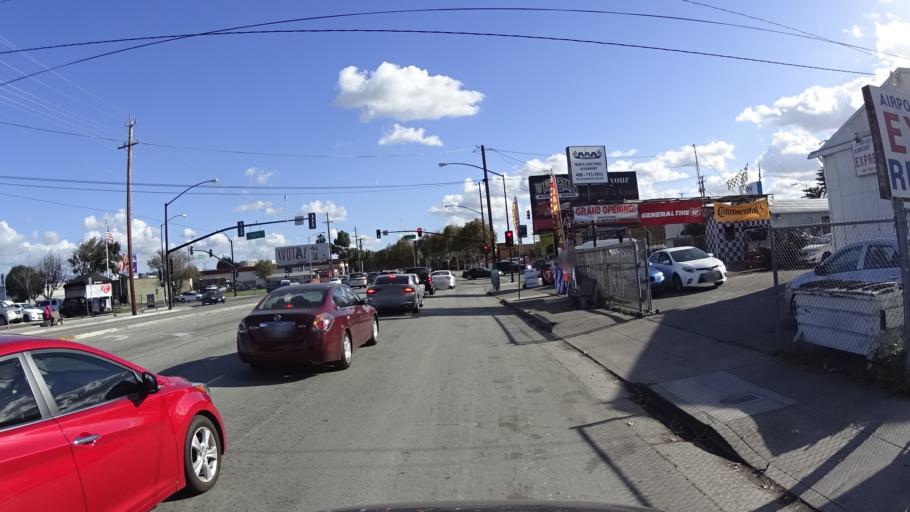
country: US
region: California
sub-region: Santa Clara County
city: San Jose
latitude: 37.3428
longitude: -121.9115
